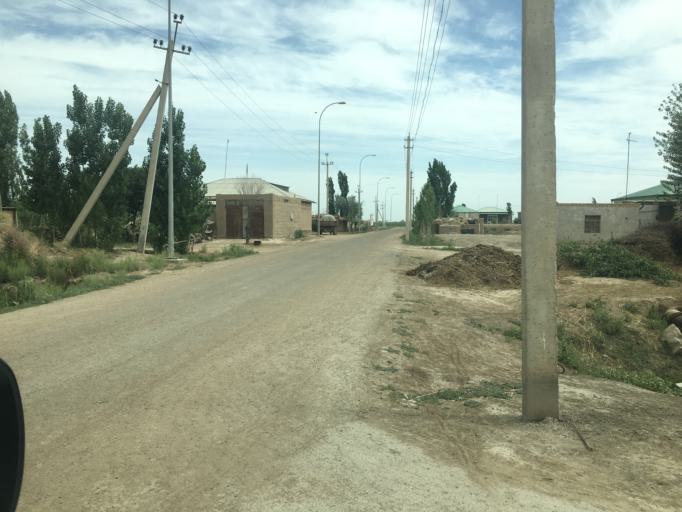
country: TM
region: Dasoguz
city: Tagta
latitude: 41.6011
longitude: 59.8521
